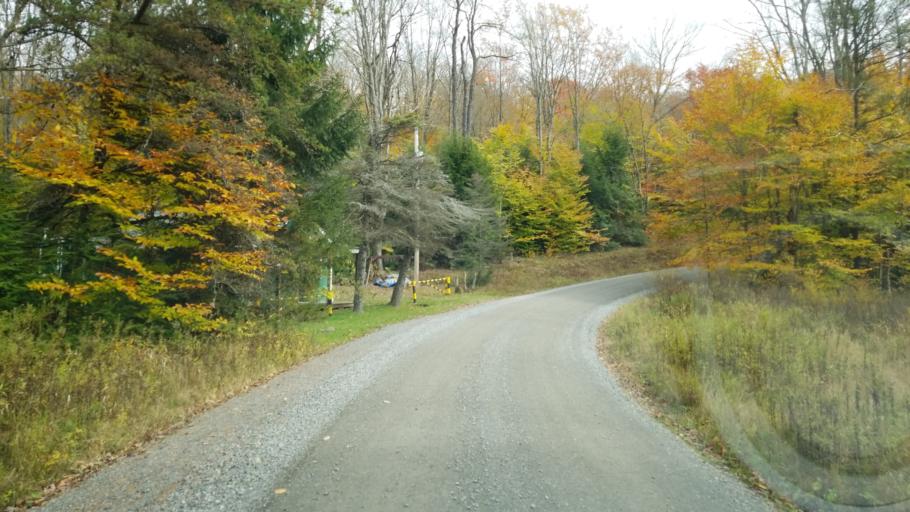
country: US
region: Pennsylvania
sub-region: Clearfield County
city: Clearfield
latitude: 41.1960
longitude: -78.4028
